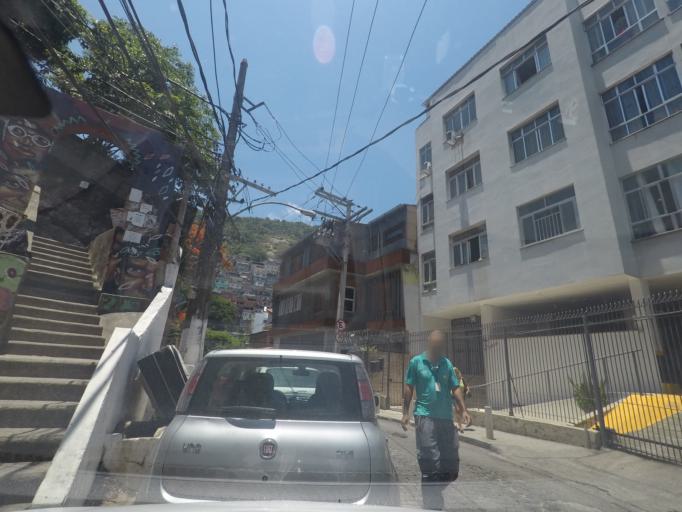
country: BR
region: Rio de Janeiro
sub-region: Rio De Janeiro
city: Rio de Janeiro
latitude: -22.9823
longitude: -43.1960
